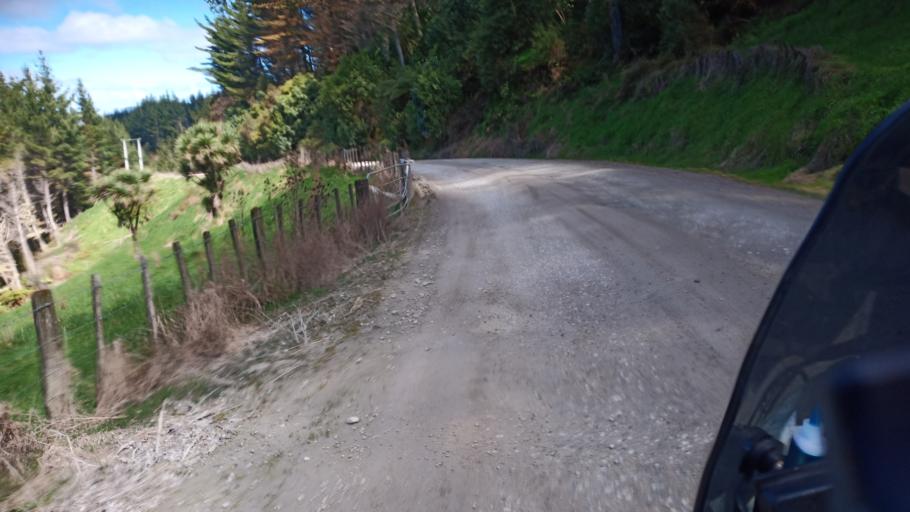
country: NZ
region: Gisborne
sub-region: Gisborne District
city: Gisborne
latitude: -38.8122
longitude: 177.7643
